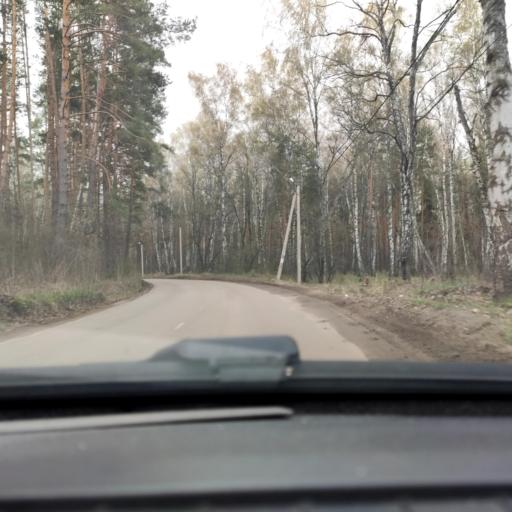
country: RU
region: Voronezj
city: Podgornoye
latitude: 51.7535
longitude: 39.1535
